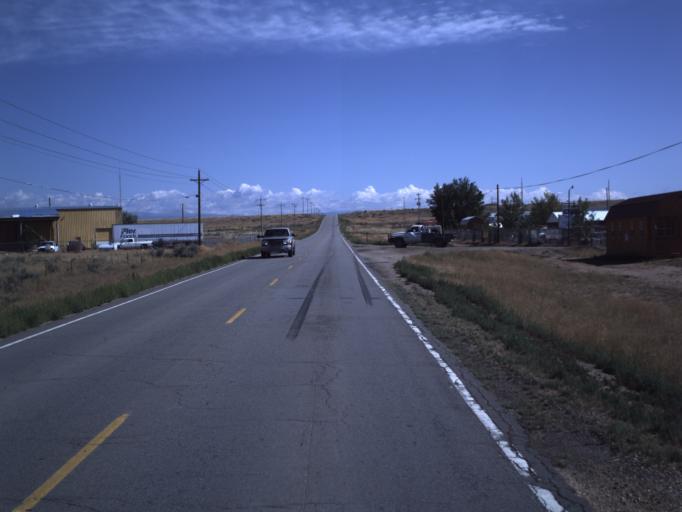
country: US
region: Utah
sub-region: Duchesne County
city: Duchesne
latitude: 40.1893
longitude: -110.3945
